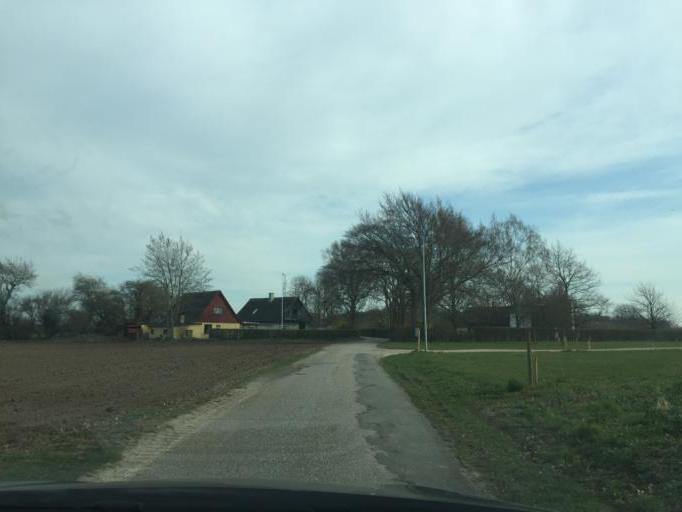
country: DK
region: South Denmark
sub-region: Faaborg-Midtfyn Kommune
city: Arslev
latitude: 55.3249
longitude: 10.5065
